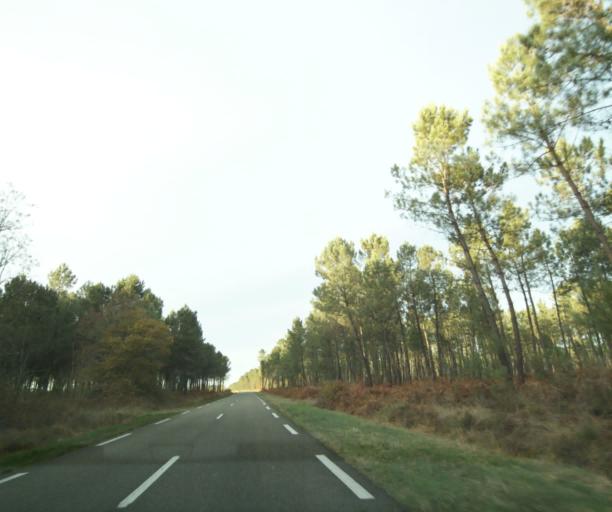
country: FR
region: Aquitaine
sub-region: Departement des Landes
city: Roquefort
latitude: 44.1666
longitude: -0.1371
